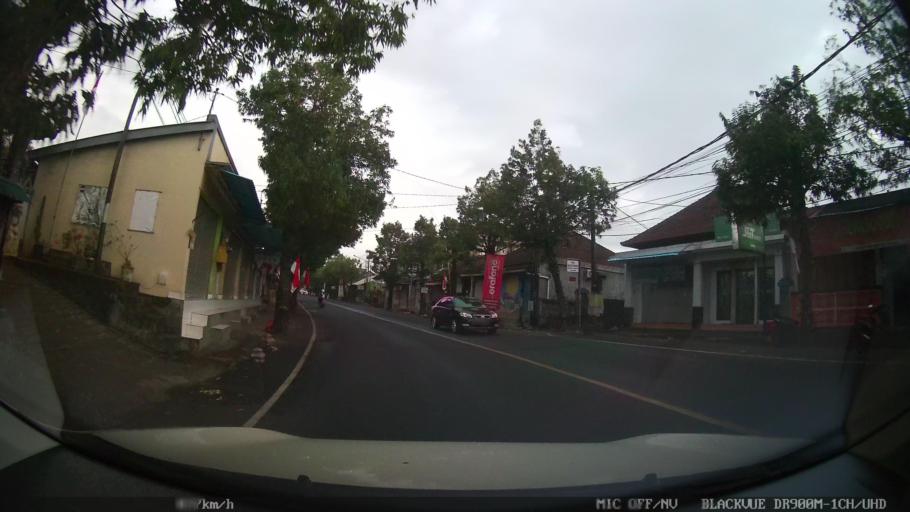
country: ID
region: Bali
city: Banjar Pasekan
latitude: -8.6022
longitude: 115.2830
